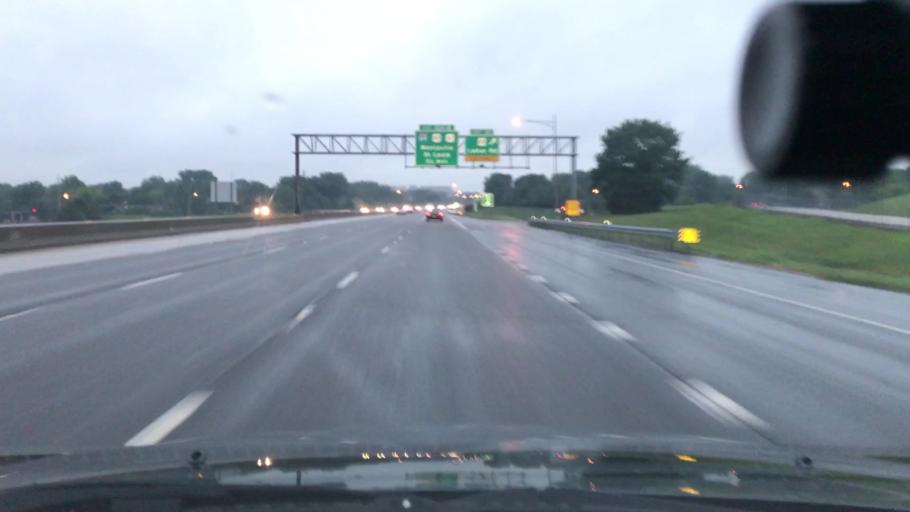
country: US
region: Missouri
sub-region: Saint Louis County
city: Creve Coeur
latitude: 38.6588
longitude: -90.4485
